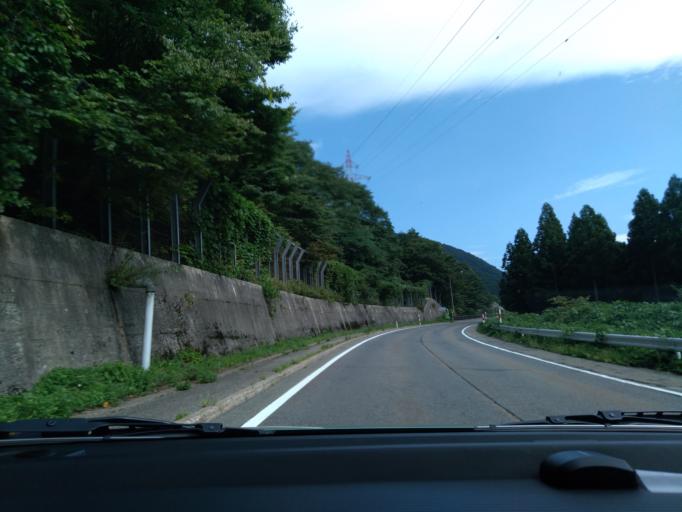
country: JP
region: Akita
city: Kakunodatemachi
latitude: 39.7036
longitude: 140.7526
